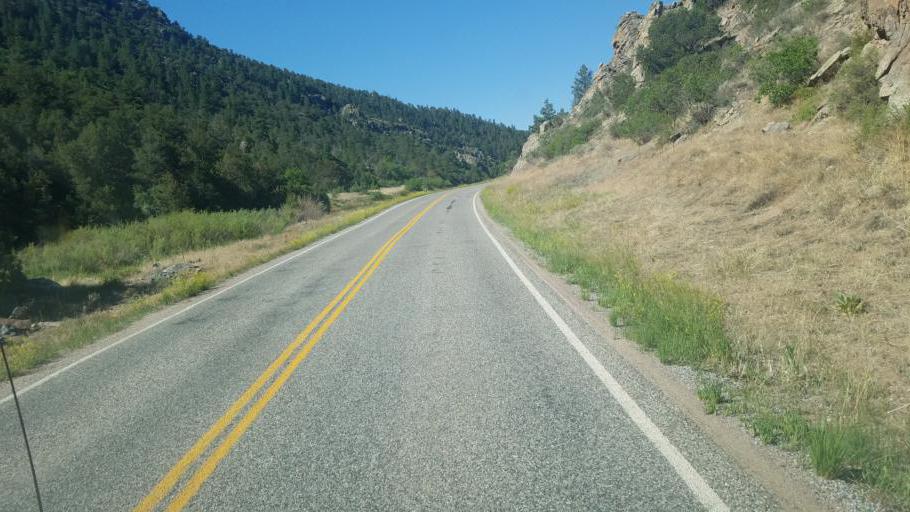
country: US
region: Colorado
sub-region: Fremont County
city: Canon City
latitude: 38.3958
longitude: -105.4469
